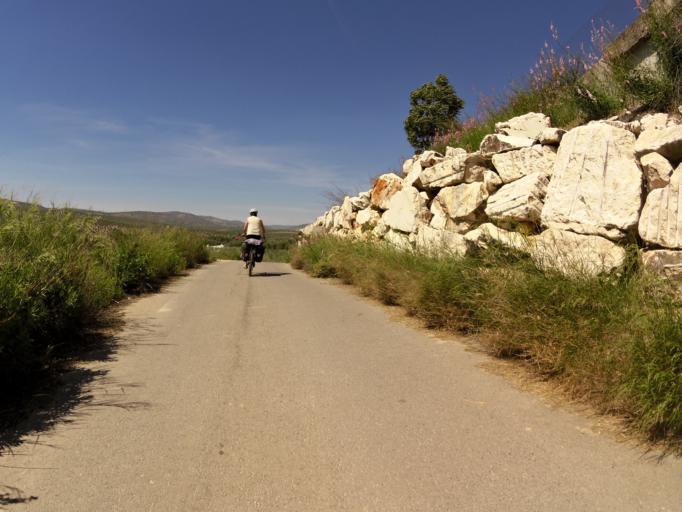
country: ES
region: Andalusia
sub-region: Provincia de Granada
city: Salar
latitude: 37.1737
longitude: -4.0825
